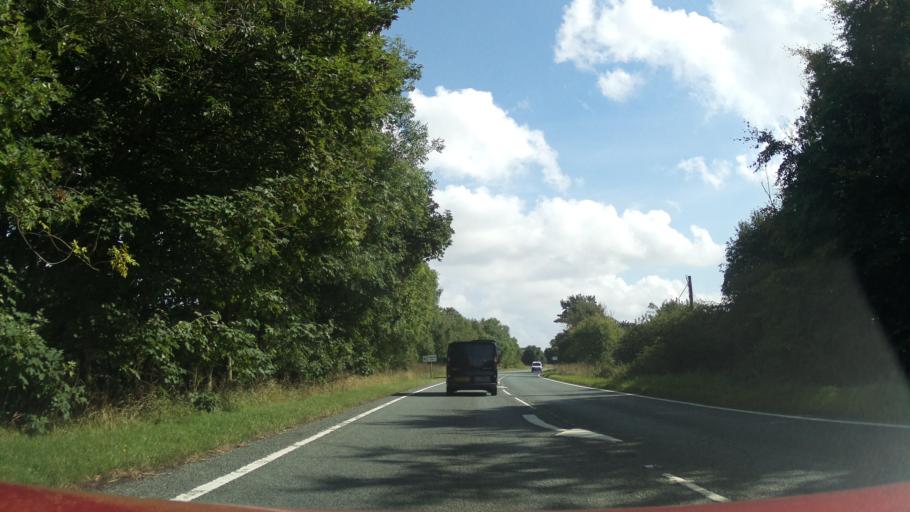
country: GB
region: England
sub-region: County Durham
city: Bishop Auckland
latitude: 54.6130
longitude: -1.6876
